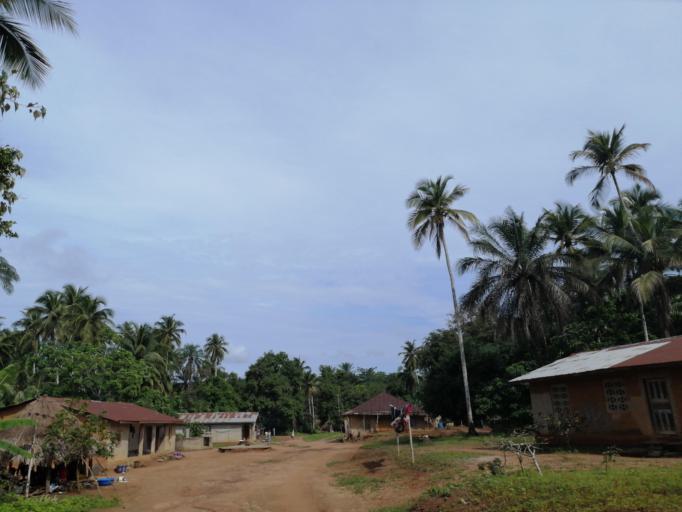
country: SL
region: Northern Province
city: Port Loko
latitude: 8.7894
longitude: -12.9282
